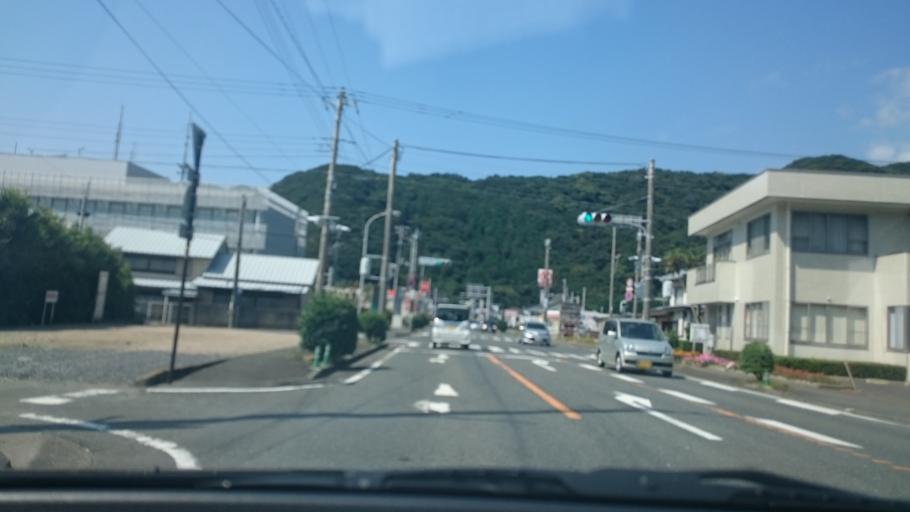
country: JP
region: Shizuoka
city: Heda
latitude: 34.8480
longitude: 138.7769
